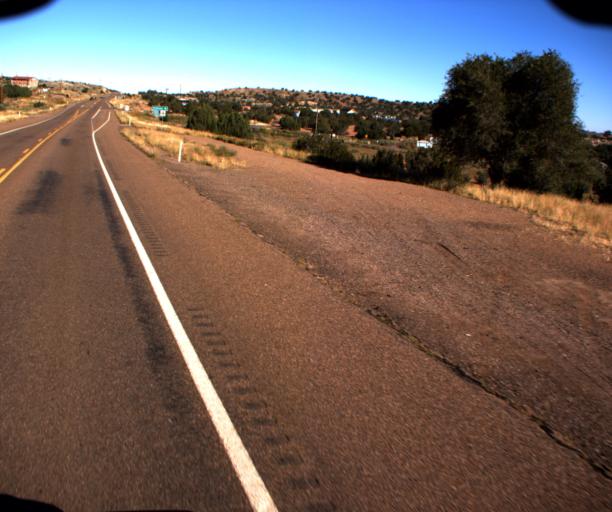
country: US
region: Arizona
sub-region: Navajo County
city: Taylor
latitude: 34.4045
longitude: -110.0753
